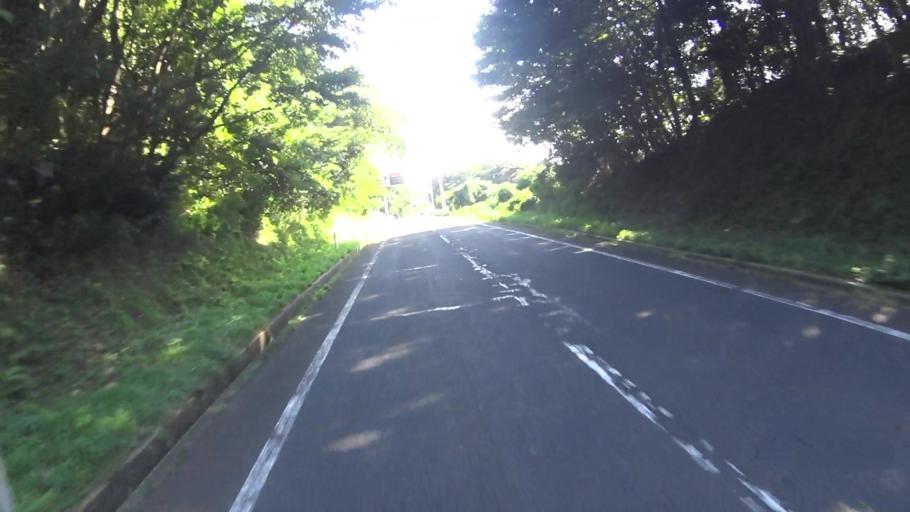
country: JP
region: Kyoto
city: Miyazu
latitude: 35.7089
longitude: 135.0695
